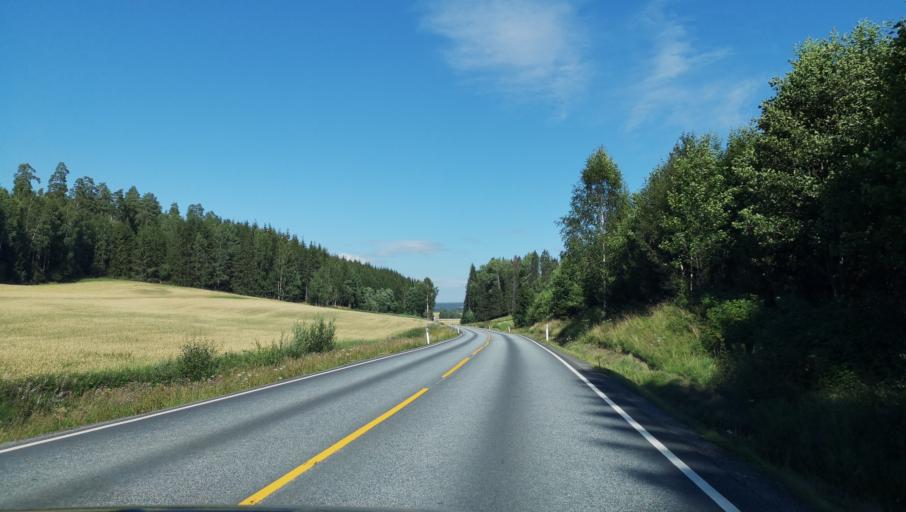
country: NO
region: Ostfold
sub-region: Hobol
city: Elvestad
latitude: 59.5888
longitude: 10.8820
